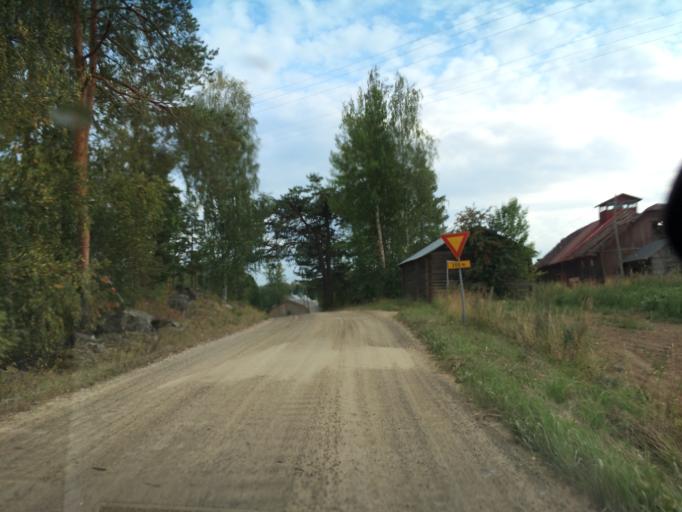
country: FI
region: Pirkanmaa
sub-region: Tampere
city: Luopioinen
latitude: 61.2588
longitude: 24.7071
